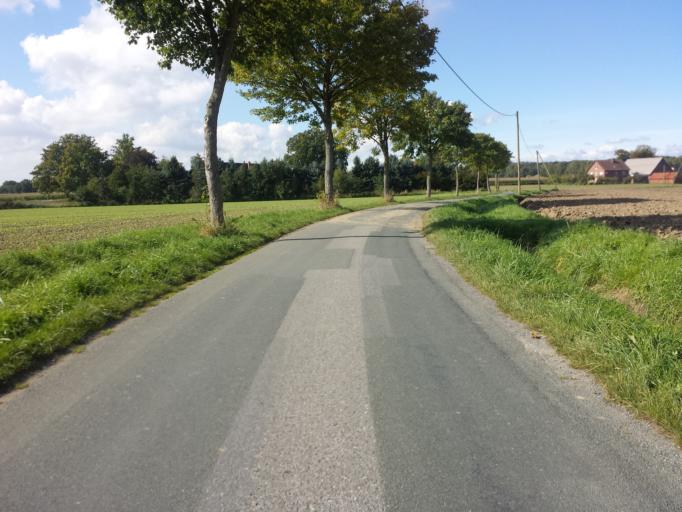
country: DE
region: North Rhine-Westphalia
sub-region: Regierungsbezirk Detmold
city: Langenberg
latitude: 51.7658
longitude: 8.3074
